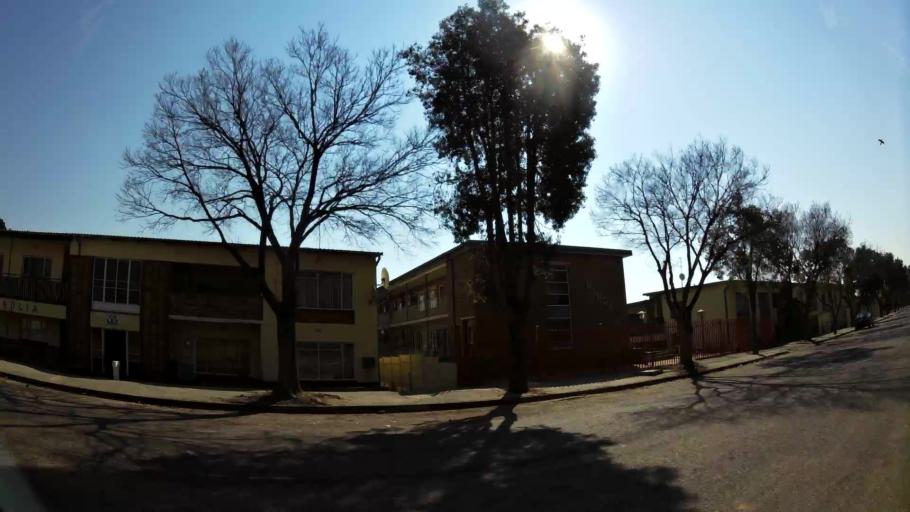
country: ZA
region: Gauteng
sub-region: Ekurhuleni Metropolitan Municipality
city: Boksburg
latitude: -26.2422
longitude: 28.2528
